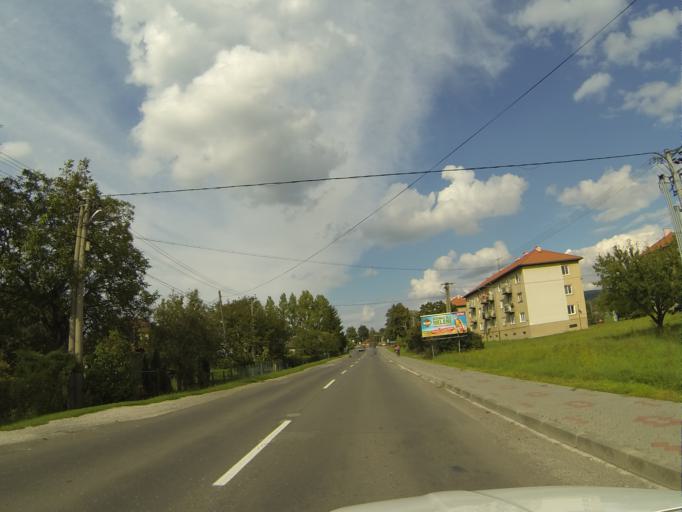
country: SK
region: Nitriansky
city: Novaky
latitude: 48.6823
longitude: 18.5217
